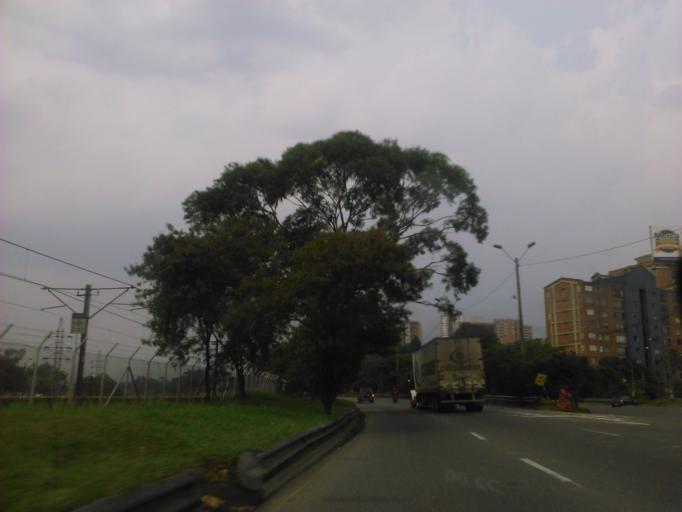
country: CO
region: Antioquia
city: Envigado
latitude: 6.1877
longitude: -75.5839
